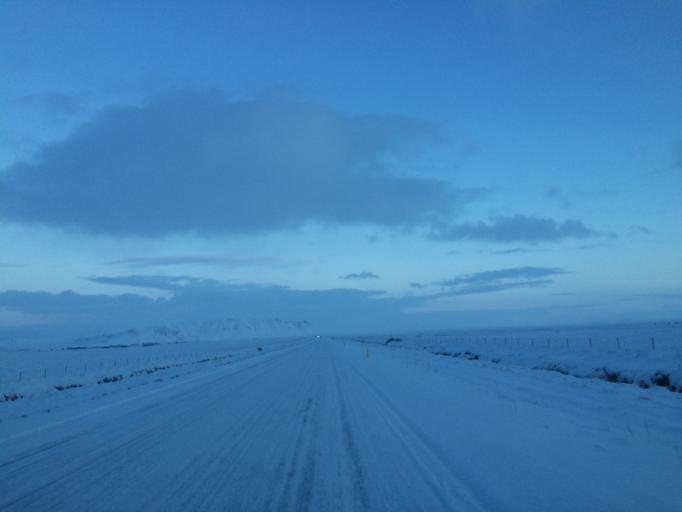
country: IS
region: South
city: Selfoss
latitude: 63.8746
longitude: -21.0945
